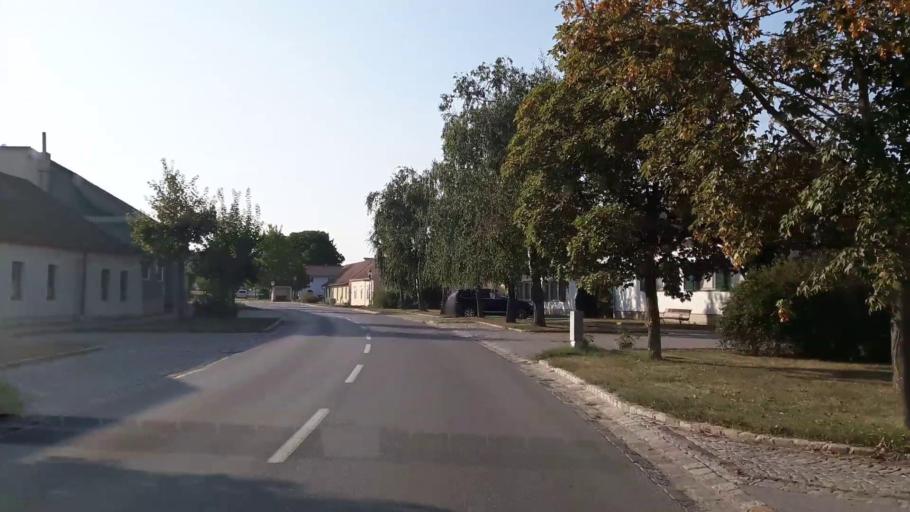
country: AT
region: Lower Austria
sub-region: Politischer Bezirk Bruck an der Leitha
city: Bruck an der Leitha
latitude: 48.0665
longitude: 16.7066
